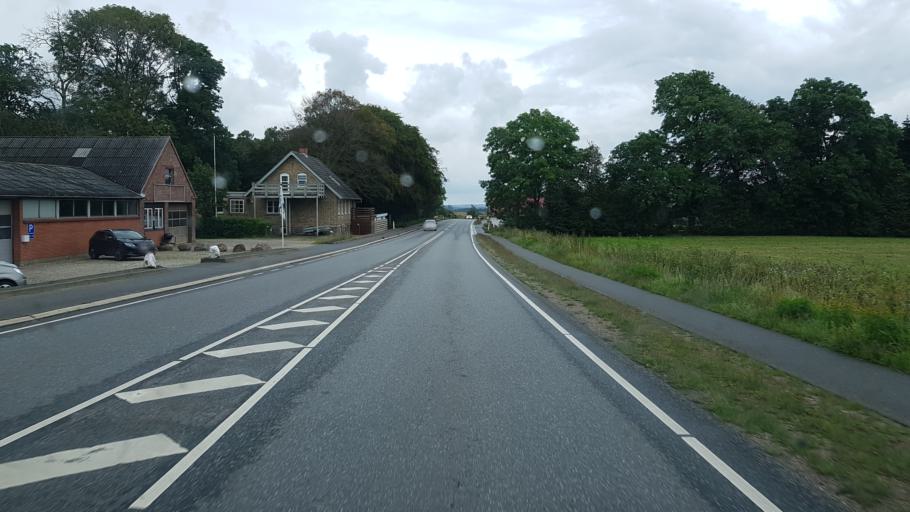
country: DK
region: Central Jutland
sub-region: Horsens Kommune
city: Horsens
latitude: 55.9075
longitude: 9.7280
